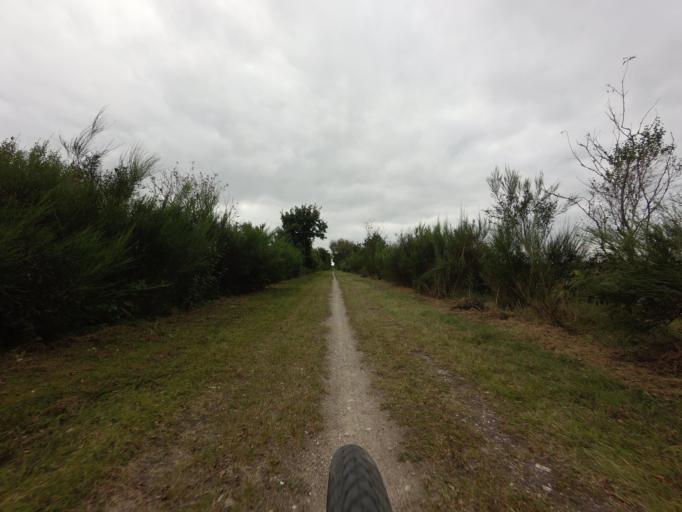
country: DK
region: Central Jutland
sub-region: Ikast-Brande Kommune
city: Brande
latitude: 55.8990
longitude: 9.0747
